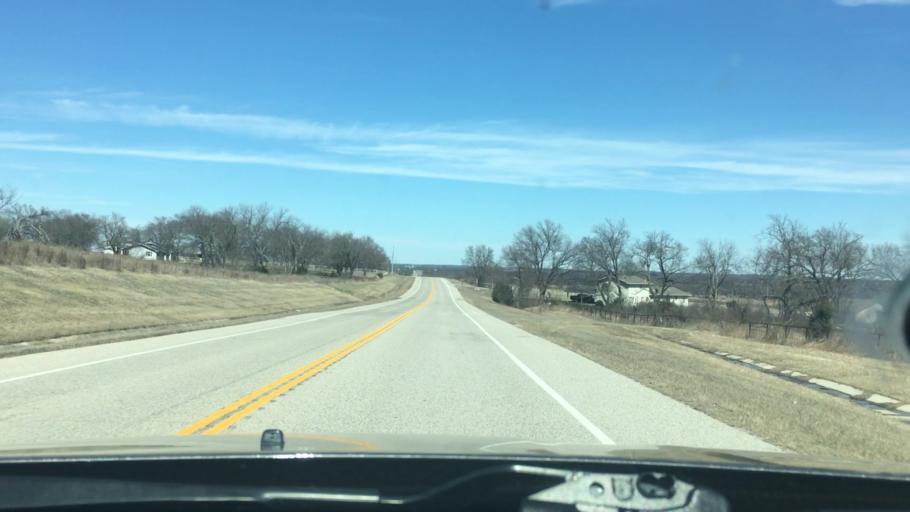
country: US
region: Oklahoma
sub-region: Carter County
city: Dickson
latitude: 34.3435
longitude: -96.9509
